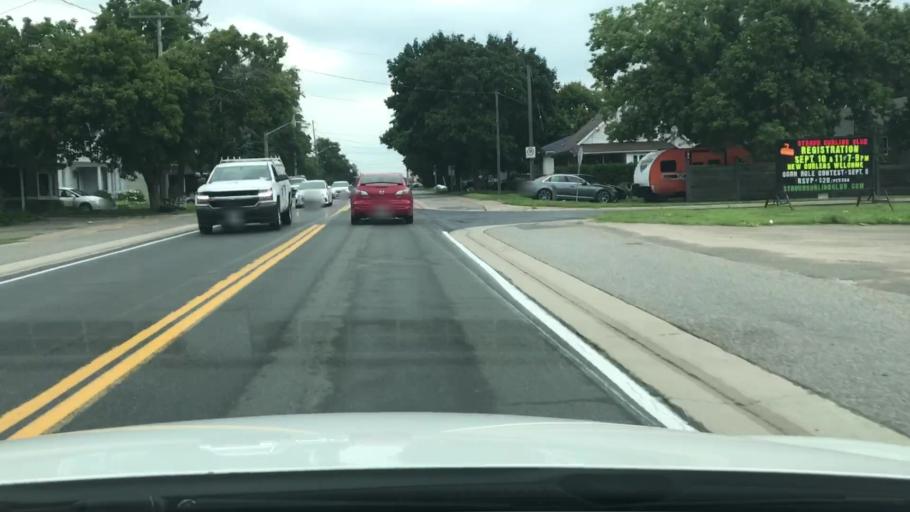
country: CA
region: Ontario
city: Innisfil
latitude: 44.3217
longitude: -79.6186
